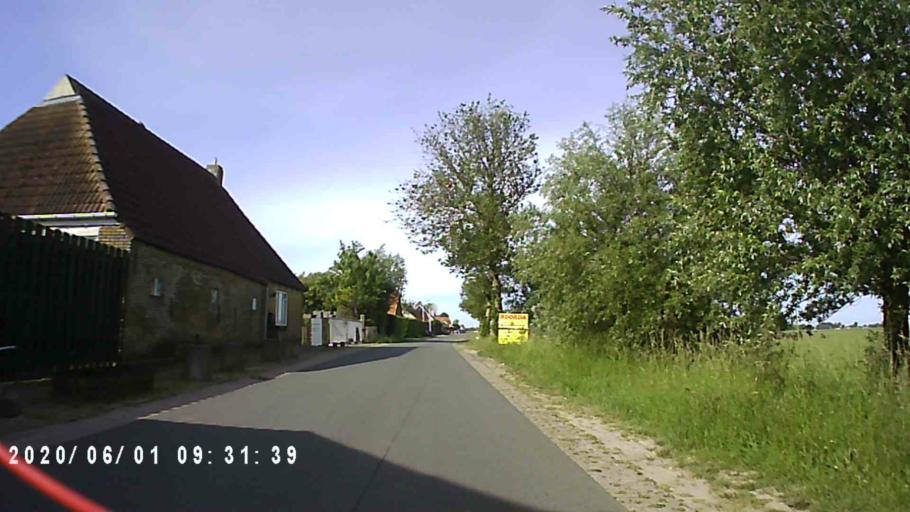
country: NL
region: Friesland
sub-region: Gemeente Leeuwarderadeel
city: Stiens
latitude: 53.2629
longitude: 5.7327
